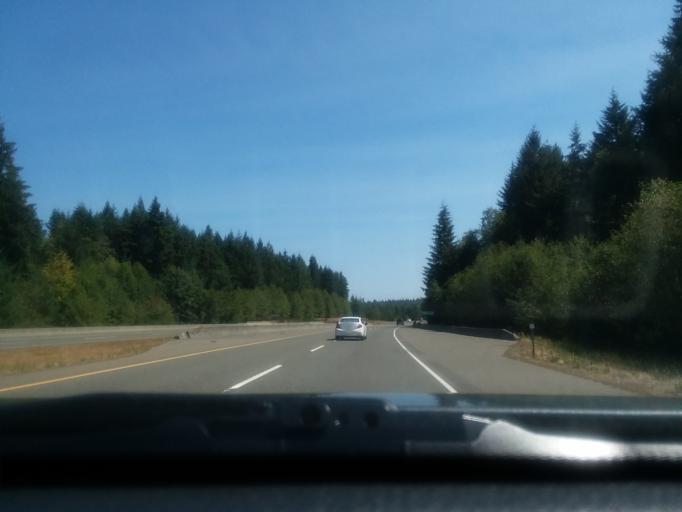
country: CA
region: British Columbia
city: Port Alberni
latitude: 49.4192
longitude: -124.7048
